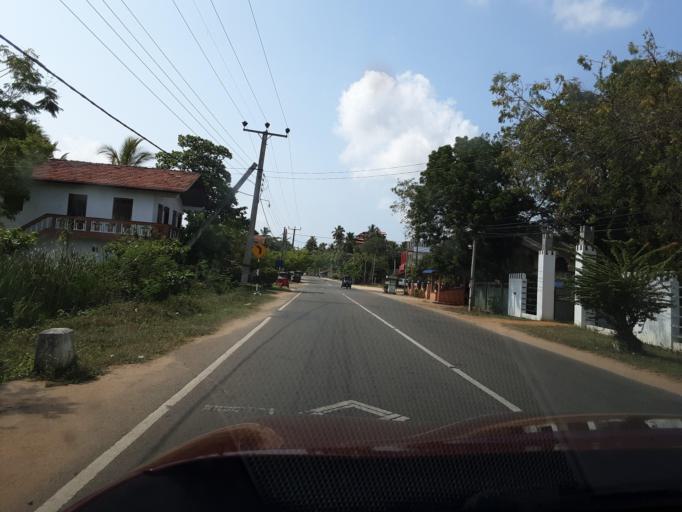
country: LK
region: Southern
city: Tangalla
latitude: 6.3028
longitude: 81.2350
